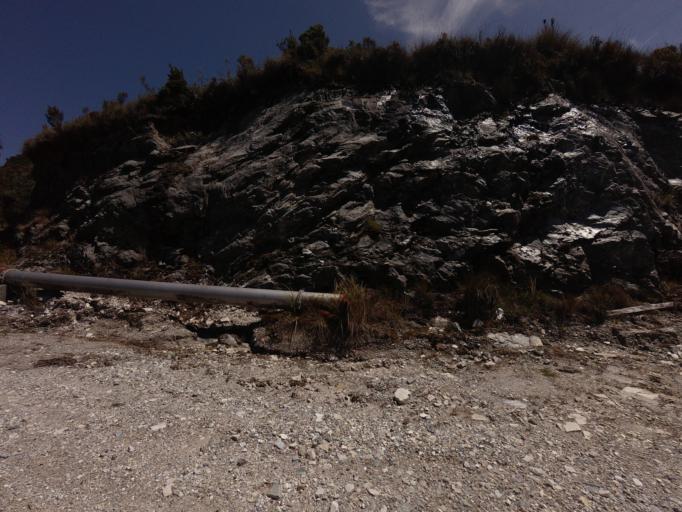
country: AU
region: Tasmania
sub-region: West Coast
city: Queenstown
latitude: -42.7350
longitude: 145.9816
